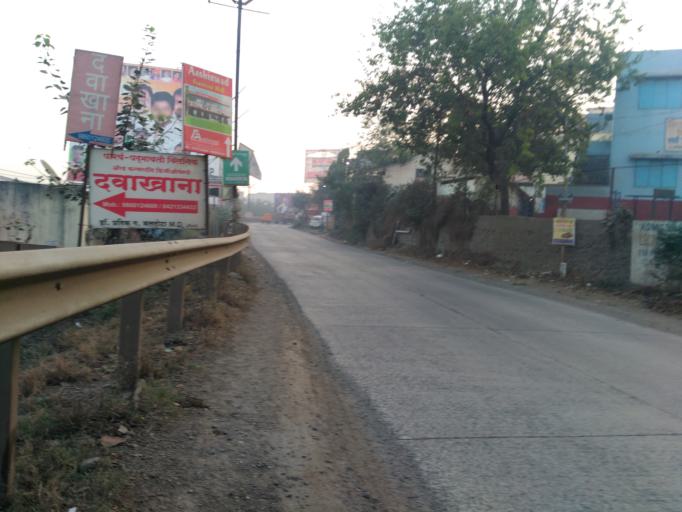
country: IN
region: Maharashtra
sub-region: Pune Division
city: Pune
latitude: 18.4496
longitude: 73.9082
